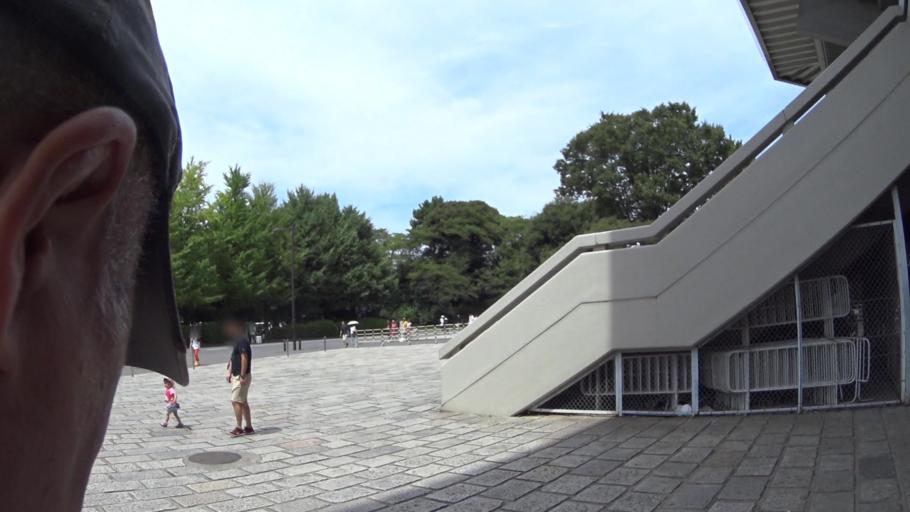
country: JP
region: Tokyo
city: Tokyo
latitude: 35.6933
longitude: 139.7493
